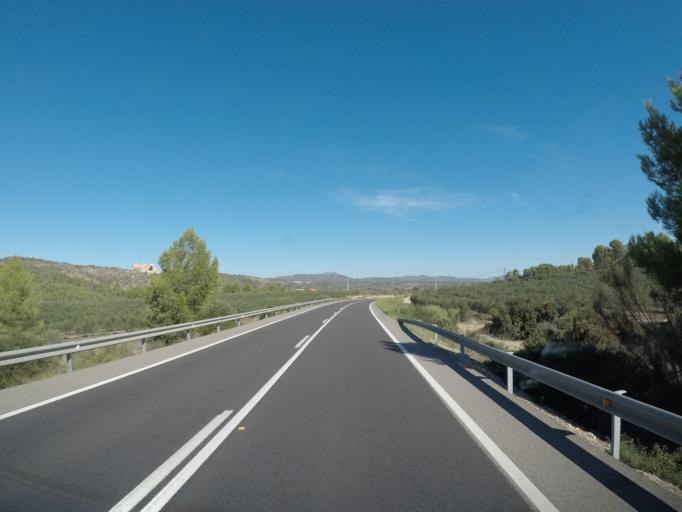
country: ES
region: Catalonia
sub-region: Provincia de Tarragona
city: Miravet
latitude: 41.0262
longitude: 0.6041
